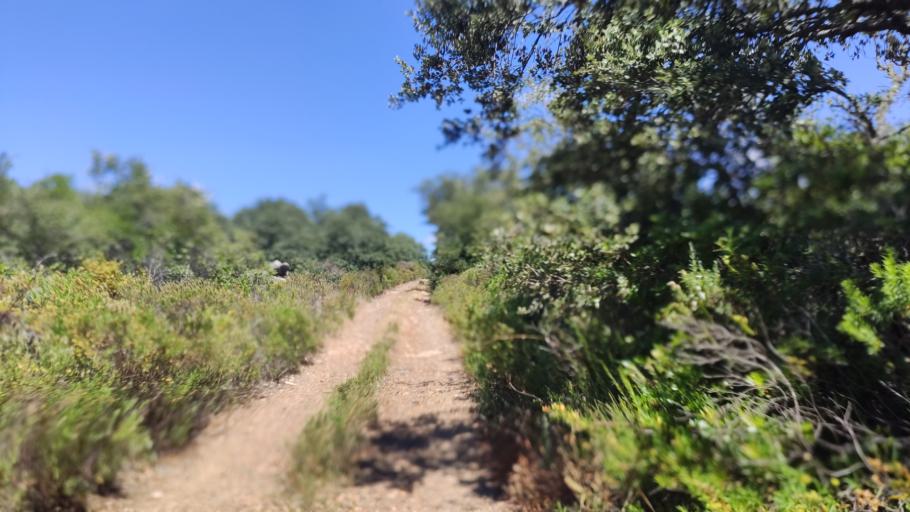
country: PT
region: Faro
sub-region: Sao Bras de Alportel
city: Sao Bras de Alportel
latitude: 37.1638
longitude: -7.9316
